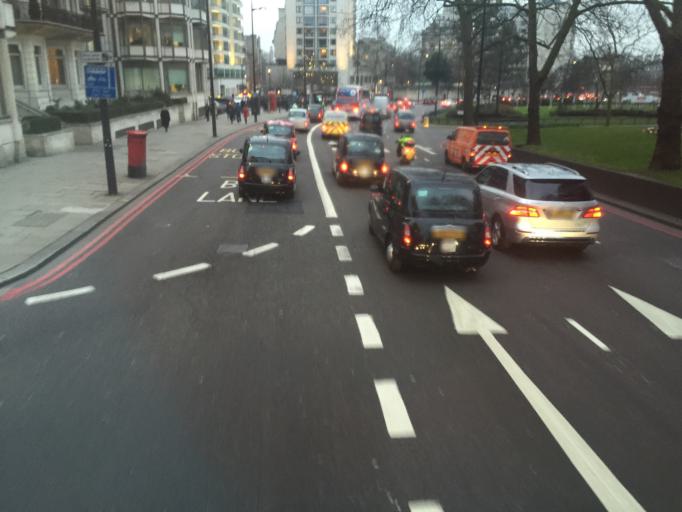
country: GB
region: England
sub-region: Greater London
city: Chelsea
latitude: 51.5062
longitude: -0.1516
